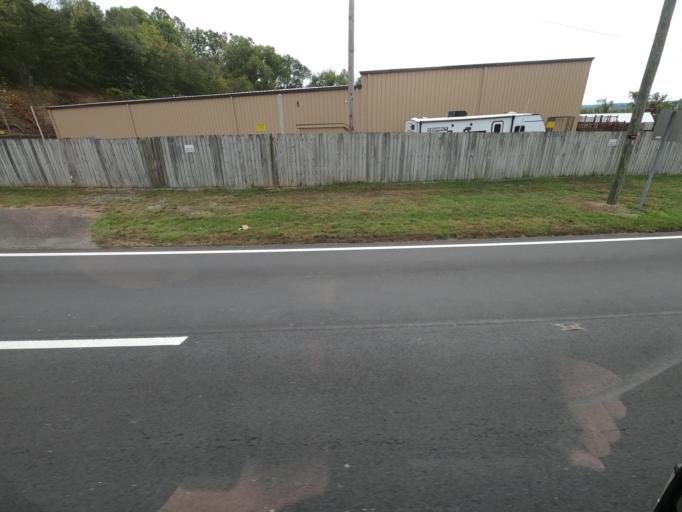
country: US
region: Tennessee
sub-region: Carter County
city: Pine Crest
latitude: 36.3266
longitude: -82.3264
